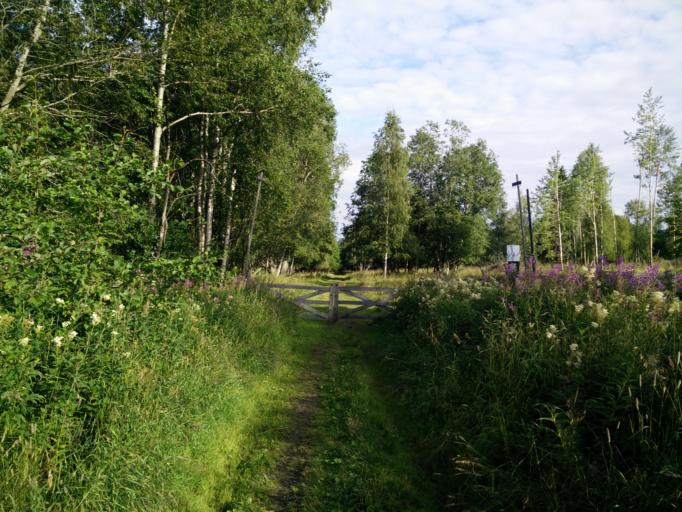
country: SE
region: Vaesternorrland
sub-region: Timra Kommun
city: Soraker
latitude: 62.4533
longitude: 17.4778
